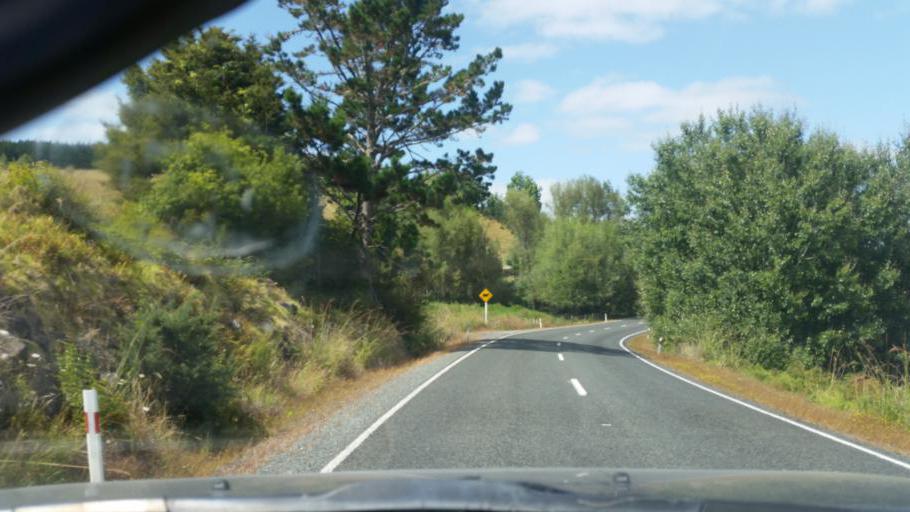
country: NZ
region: Northland
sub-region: Whangarei
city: Ruakaka
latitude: -35.9552
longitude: 174.2943
